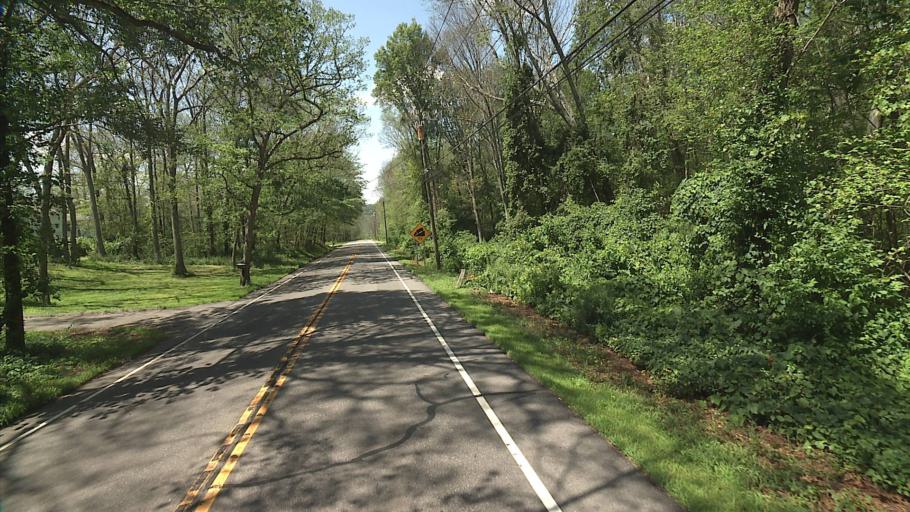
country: US
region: Connecticut
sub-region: New London County
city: Baltic
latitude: 41.7074
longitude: -72.0458
